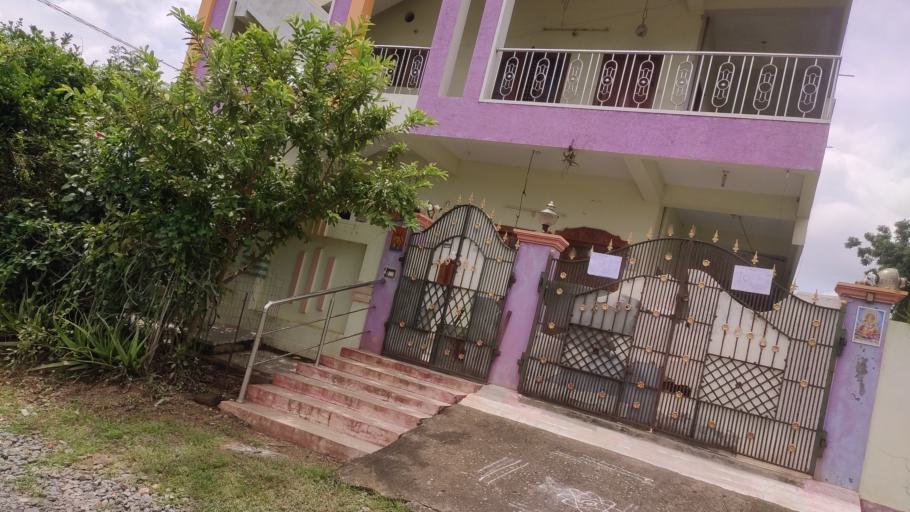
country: IN
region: Telangana
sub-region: Khammam
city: Khammam
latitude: 17.2456
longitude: 80.1934
